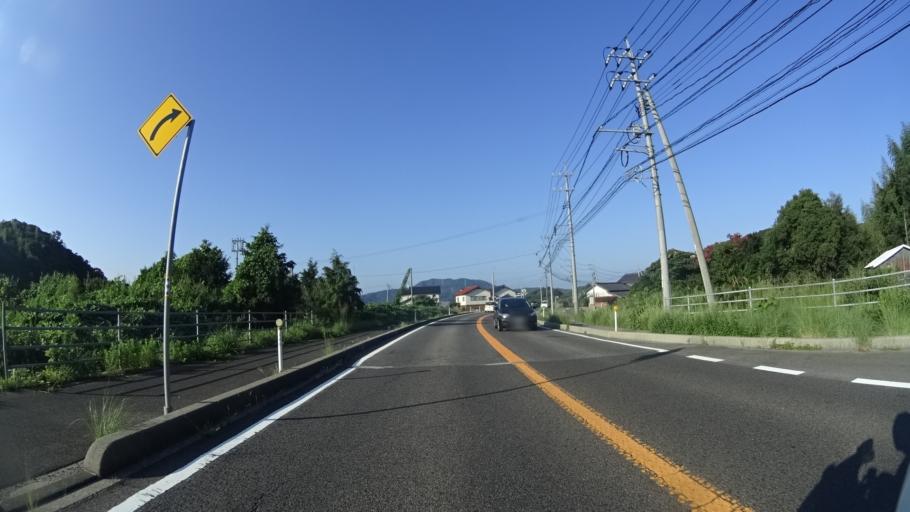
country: JP
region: Shimane
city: Sakaiminato
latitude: 35.5215
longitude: 133.1441
